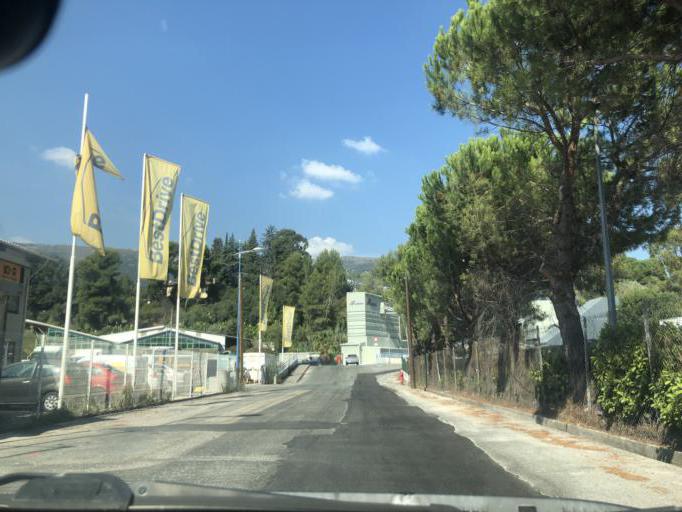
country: FR
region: Provence-Alpes-Cote d'Azur
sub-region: Departement des Alpes-Maritimes
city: Colomars
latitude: 43.7717
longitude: 7.2058
